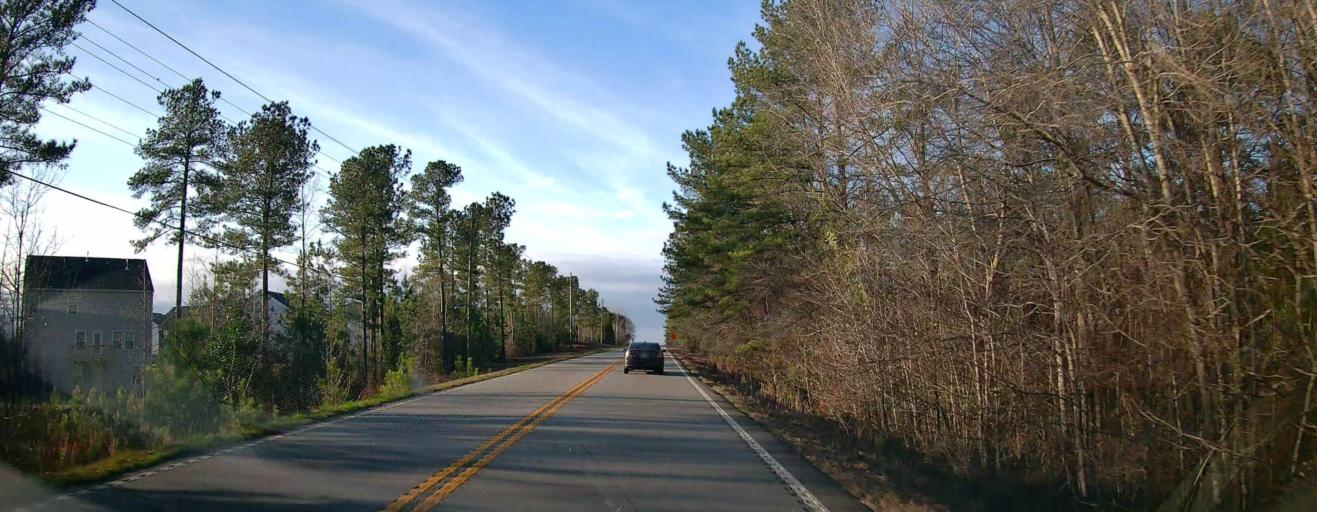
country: US
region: Georgia
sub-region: Troup County
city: West Point
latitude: 32.8673
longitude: -85.1403
